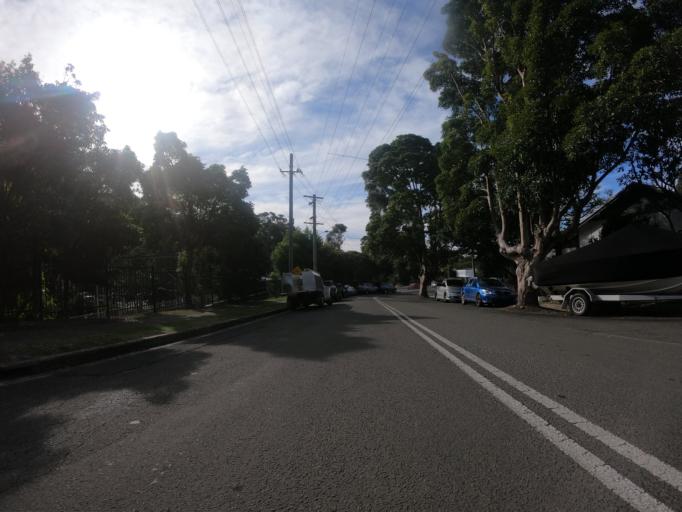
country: AU
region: New South Wales
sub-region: Wollongong
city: Bulli
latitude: -34.3070
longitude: 150.9289
